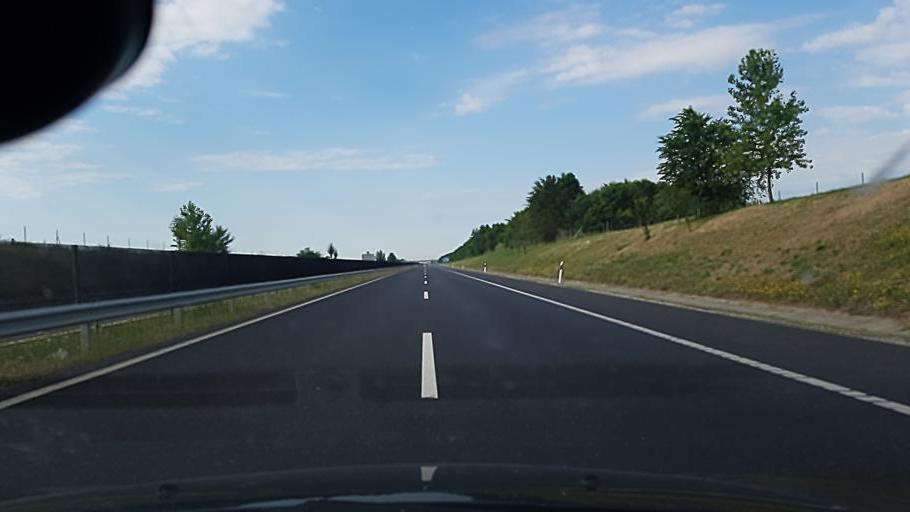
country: HU
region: Fejer
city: Rackeresztur
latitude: 47.2977
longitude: 18.8655
